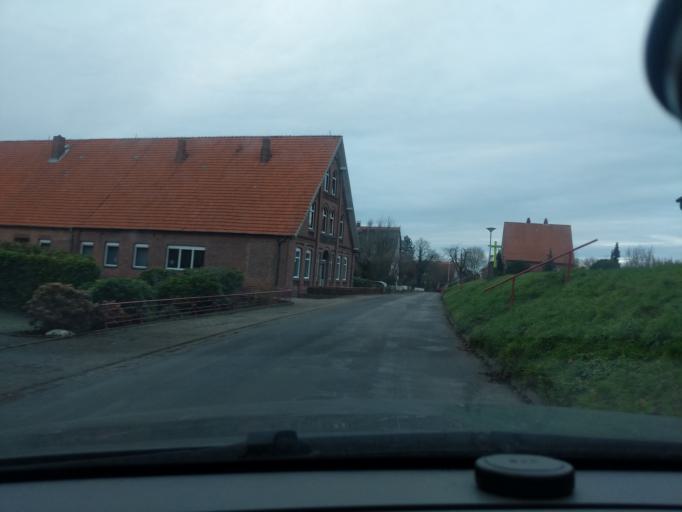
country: DE
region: Lower Saxony
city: Guderhandviertel
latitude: 53.5374
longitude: 9.6111
